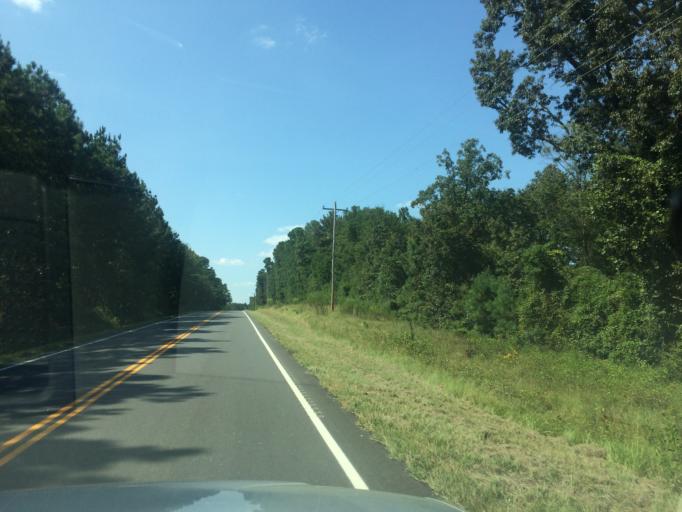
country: US
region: South Carolina
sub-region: Lexington County
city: Batesburg-Leesville
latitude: 33.7065
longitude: -81.4878
